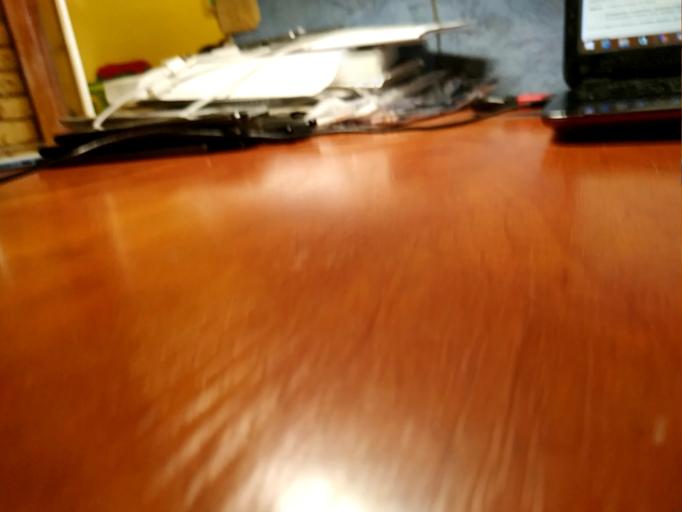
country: RU
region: Tverskaya
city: Sandovo
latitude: 58.4576
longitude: 36.4295
